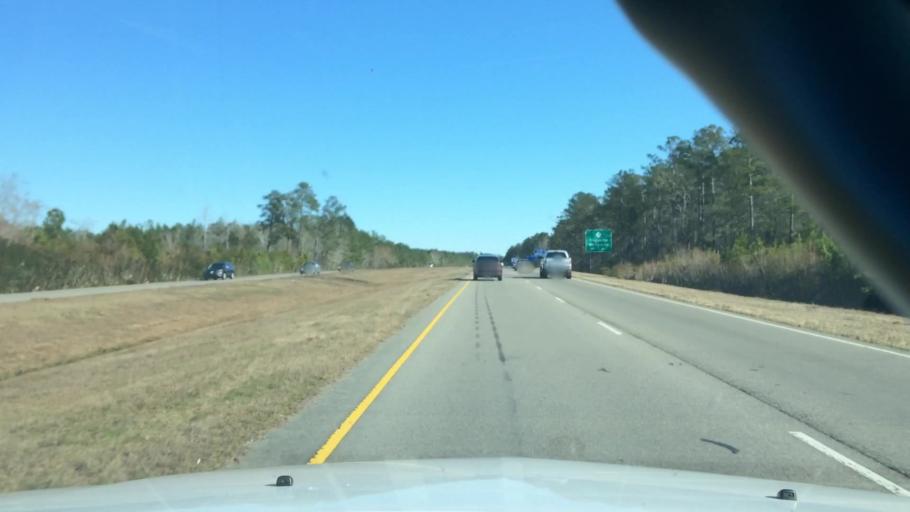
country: US
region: North Carolina
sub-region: Brunswick County
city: Shallotte
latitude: 33.9636
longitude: -78.4157
